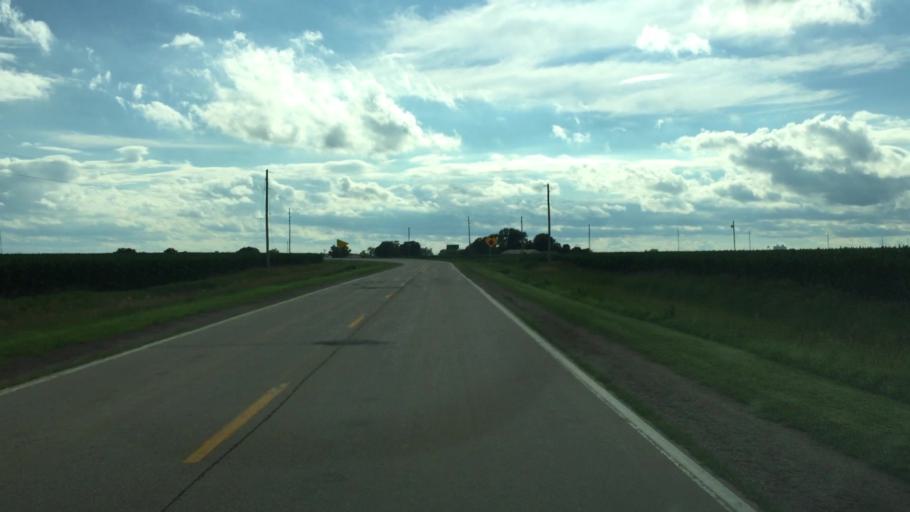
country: US
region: Iowa
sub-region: Jasper County
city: Prairie City
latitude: 41.5806
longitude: -93.1763
